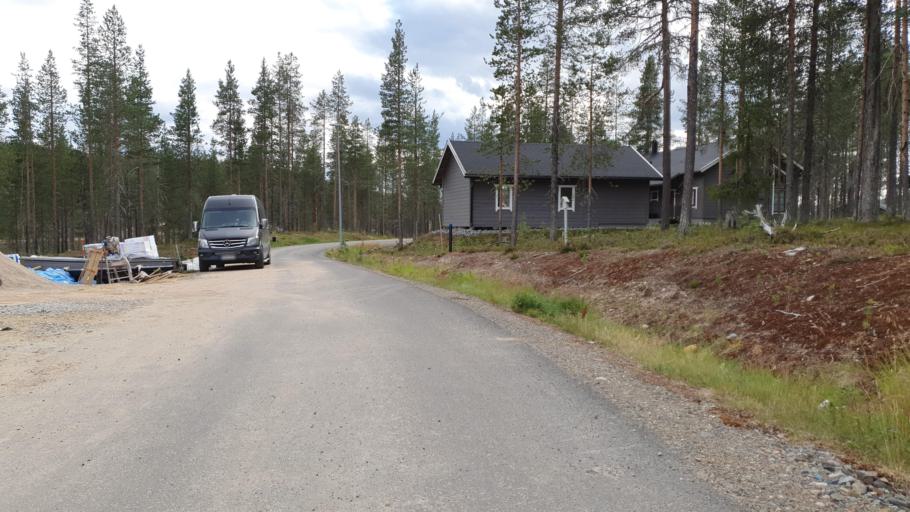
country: FI
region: Lapland
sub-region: Tunturi-Lappi
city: Kolari
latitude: 67.5943
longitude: 24.1271
